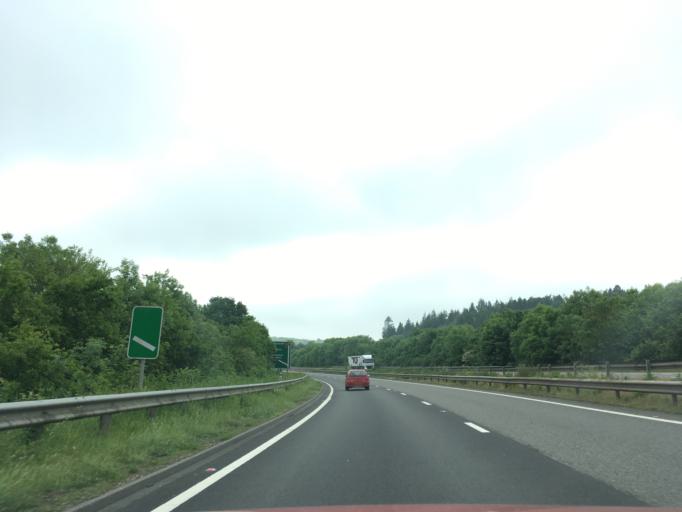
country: GB
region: England
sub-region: Devon
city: Chudleigh
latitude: 50.6001
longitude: -3.6154
